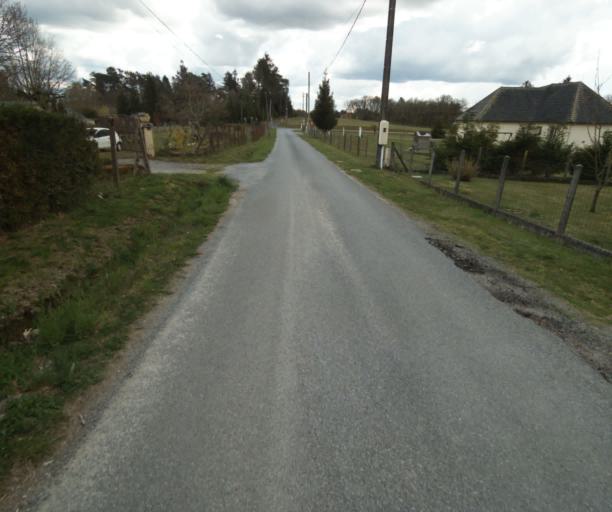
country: FR
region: Limousin
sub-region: Departement de la Correze
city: Correze
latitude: 45.2808
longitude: 1.9426
